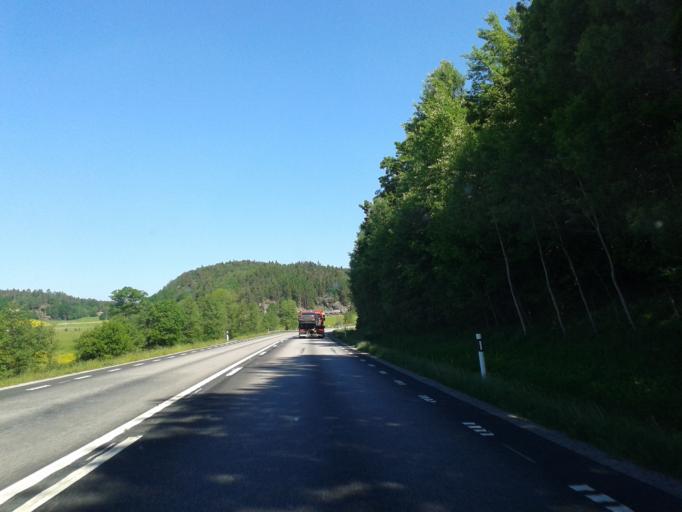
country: SE
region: Vaestra Goetaland
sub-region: Orust
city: Henan
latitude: 58.1996
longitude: 11.6896
